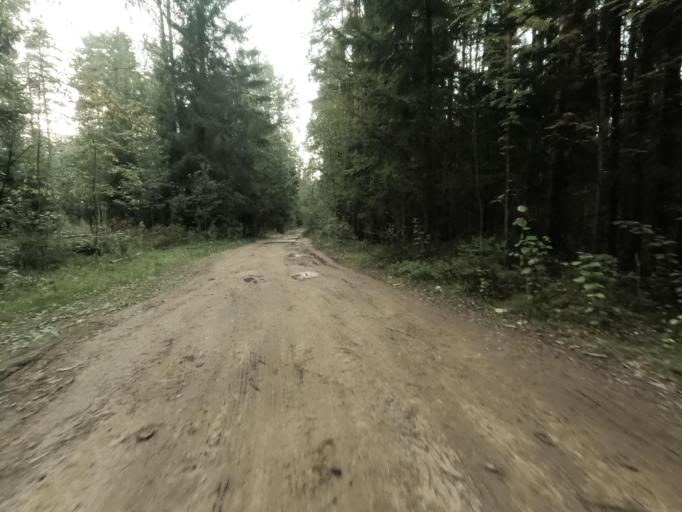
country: RU
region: Leningrad
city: Otradnoye
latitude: 59.8467
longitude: 30.7978
